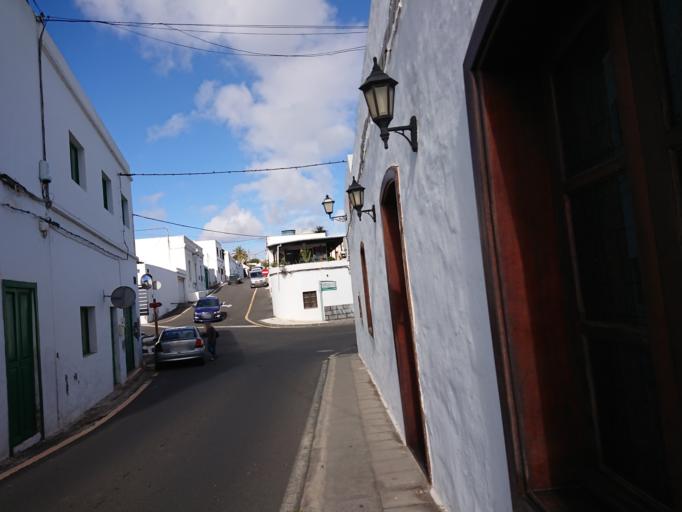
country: ES
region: Canary Islands
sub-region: Provincia de Las Palmas
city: Haria
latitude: 29.1454
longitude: -13.5015
